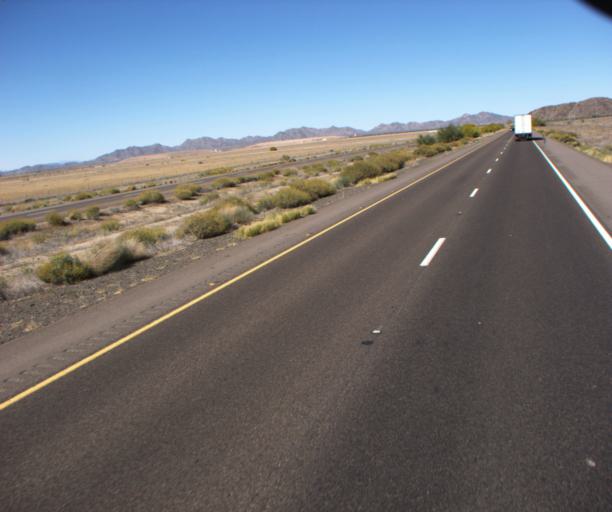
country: US
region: Arizona
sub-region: Maricopa County
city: Gila Bend
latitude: 33.1479
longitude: -112.6499
